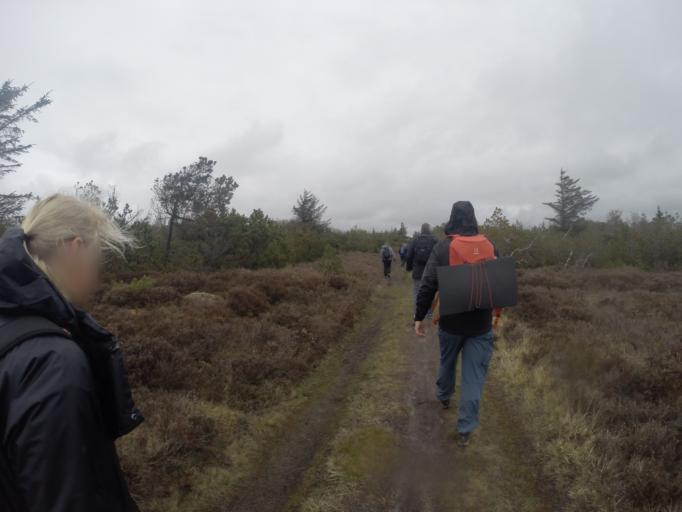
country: DK
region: North Denmark
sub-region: Thisted Kommune
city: Hurup
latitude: 56.8986
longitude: 8.3370
